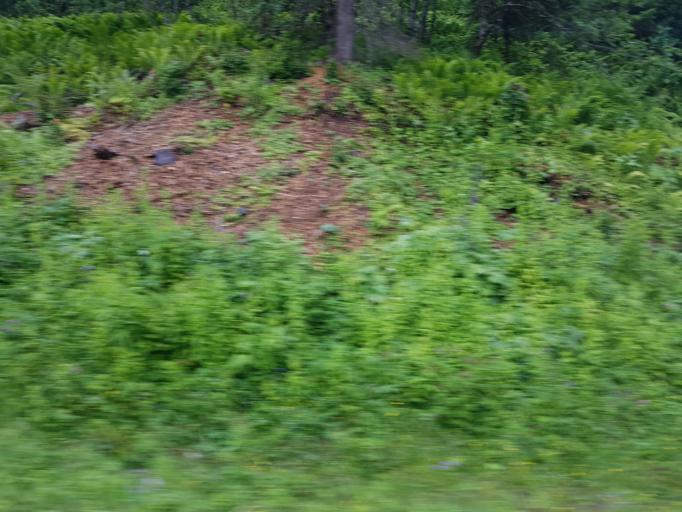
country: NO
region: Sor-Trondelag
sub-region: Selbu
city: Mebonden
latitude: 63.3150
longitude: 11.0829
